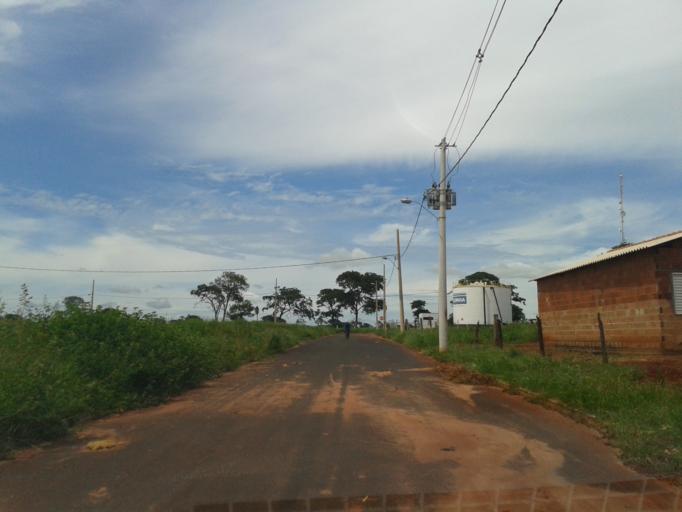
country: BR
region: Minas Gerais
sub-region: Santa Vitoria
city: Santa Vitoria
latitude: -18.8351
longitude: -50.1417
